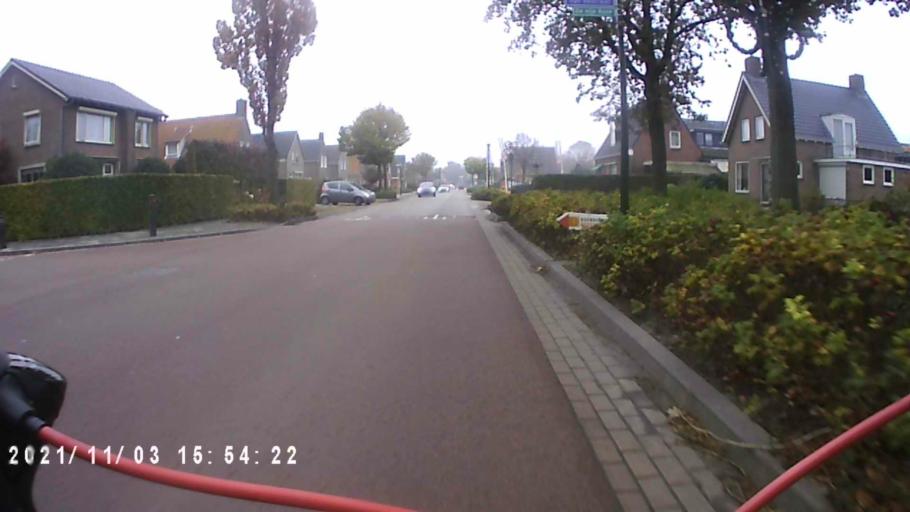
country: NL
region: Groningen
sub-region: Gemeente Leek
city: Leek
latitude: 53.0684
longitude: 6.3319
